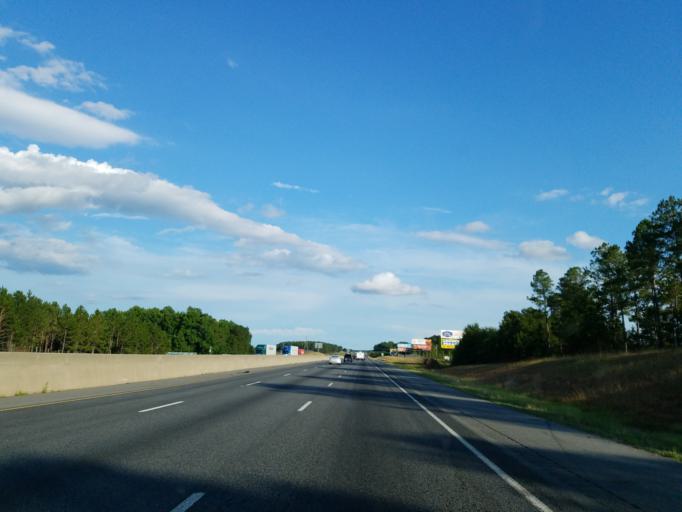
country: US
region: Georgia
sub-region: Tift County
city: Tifton
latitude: 31.5449
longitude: -83.5317
